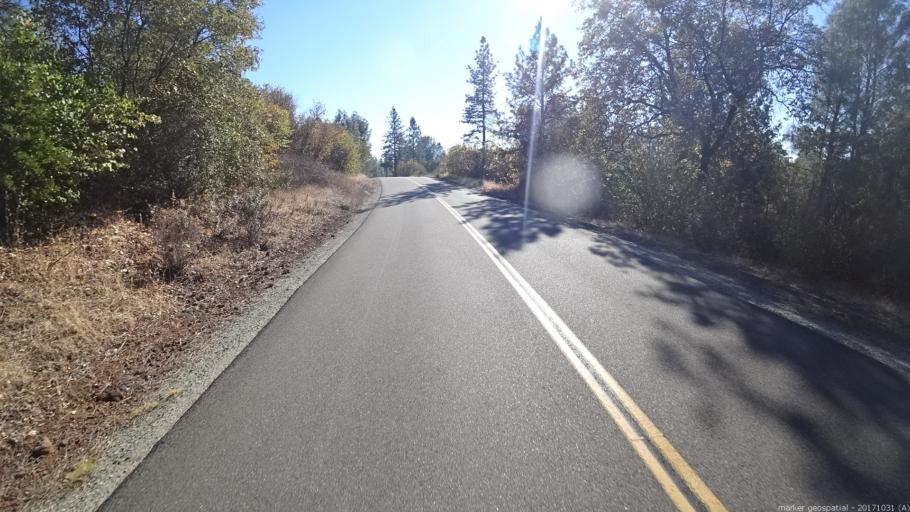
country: US
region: California
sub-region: Shasta County
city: Shingletown
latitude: 40.4553
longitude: -122.0063
